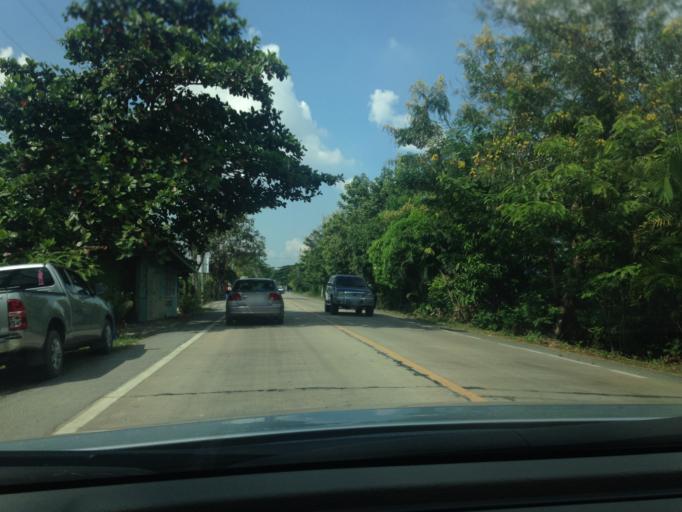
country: TH
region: Pathum Thani
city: Khlong Luang
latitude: 14.0620
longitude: 100.5891
